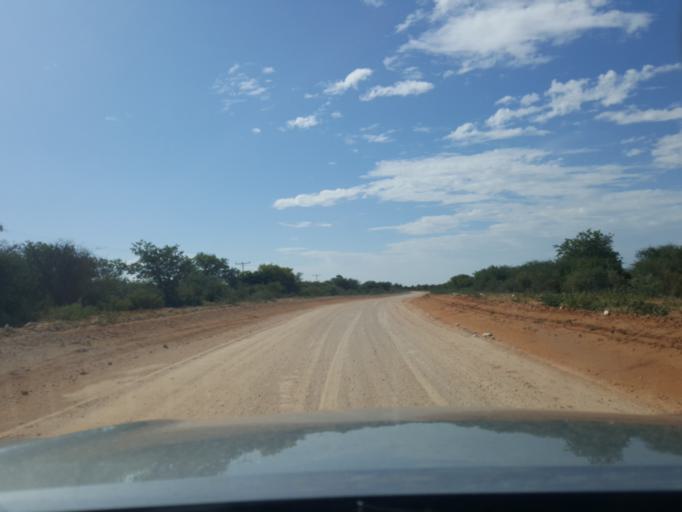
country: BW
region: Kweneng
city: Khudumelapye
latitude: -23.7762
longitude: 24.7689
